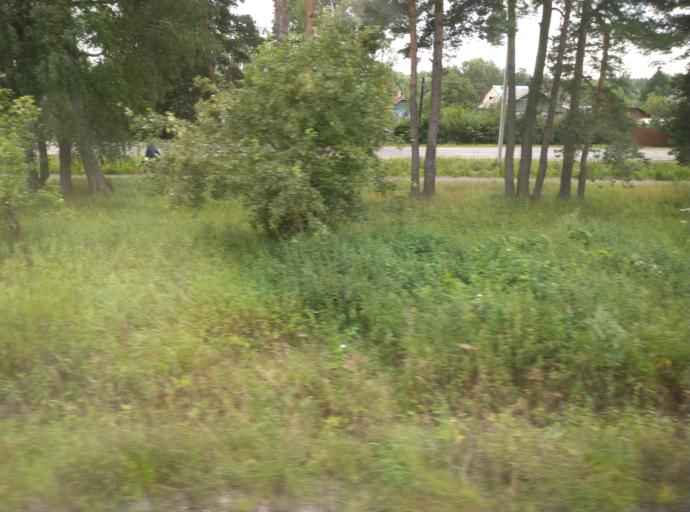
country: RU
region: Jaroslavl
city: Burmakino
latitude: 57.4371
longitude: 40.3046
